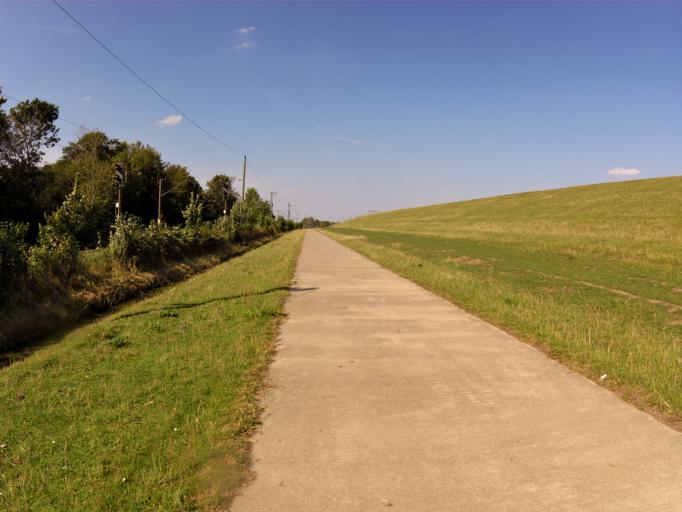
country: DE
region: Lower Saxony
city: Nordenham
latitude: 53.4463
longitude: 8.4761
